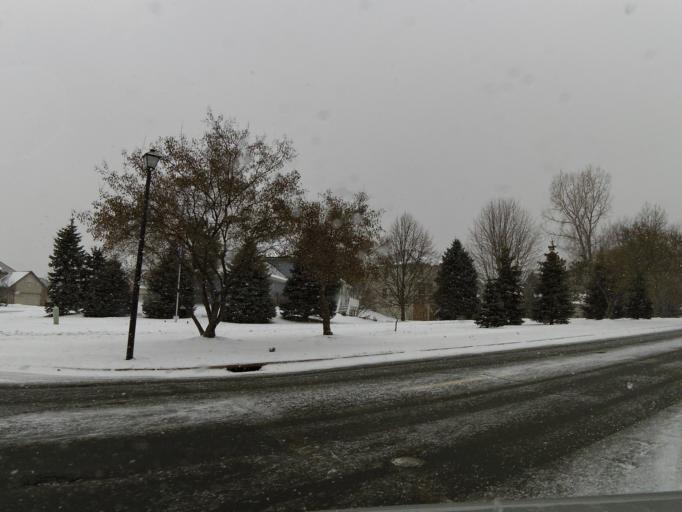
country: US
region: Minnesota
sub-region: Washington County
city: Woodbury
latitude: 44.9318
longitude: -92.9200
